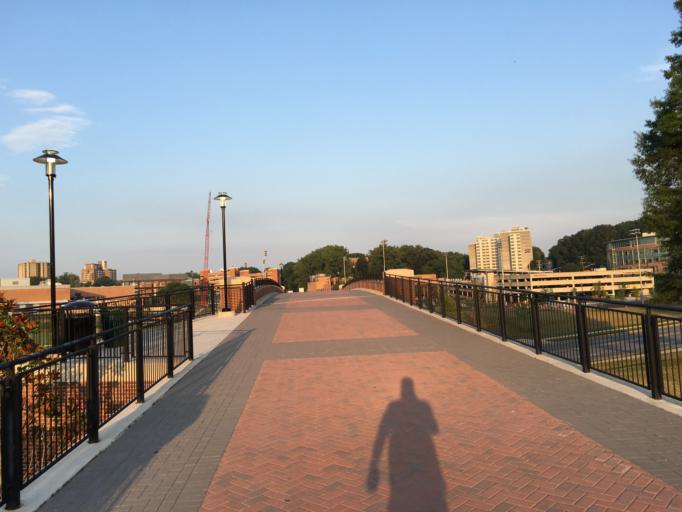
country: US
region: Maryland
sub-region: Baltimore County
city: Towson
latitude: 39.3945
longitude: -76.6158
